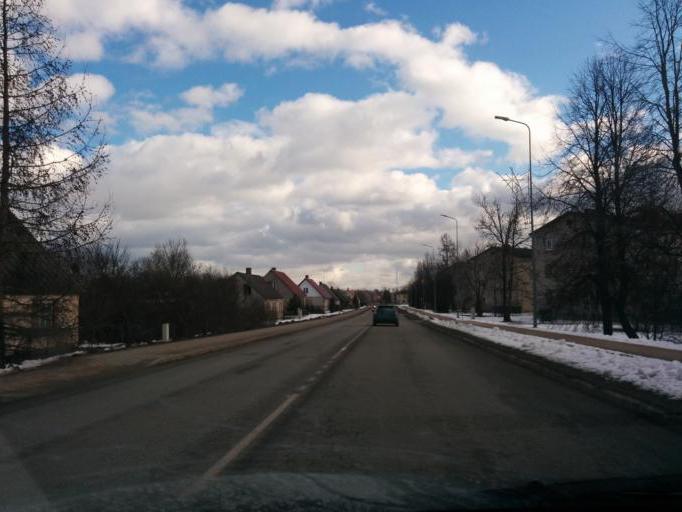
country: LV
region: Balvu Rajons
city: Balvi
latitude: 57.1407
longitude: 27.2478
